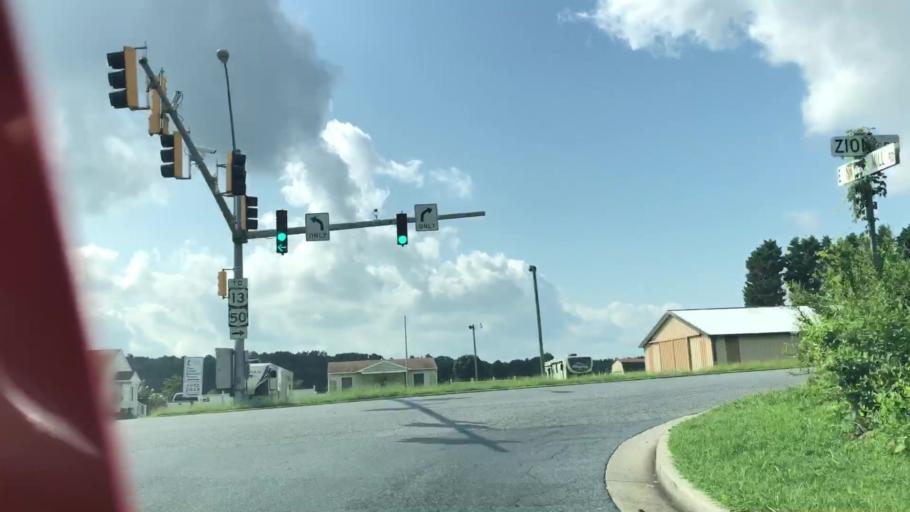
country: US
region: Maryland
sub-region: Wicomico County
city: Salisbury
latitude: 38.3949
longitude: -75.5628
